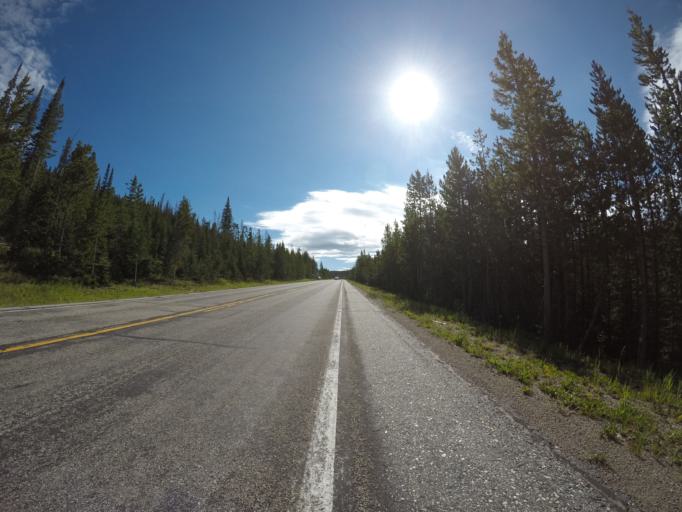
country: US
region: Wyoming
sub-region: Carbon County
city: Saratoga
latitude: 41.3230
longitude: -106.4539
